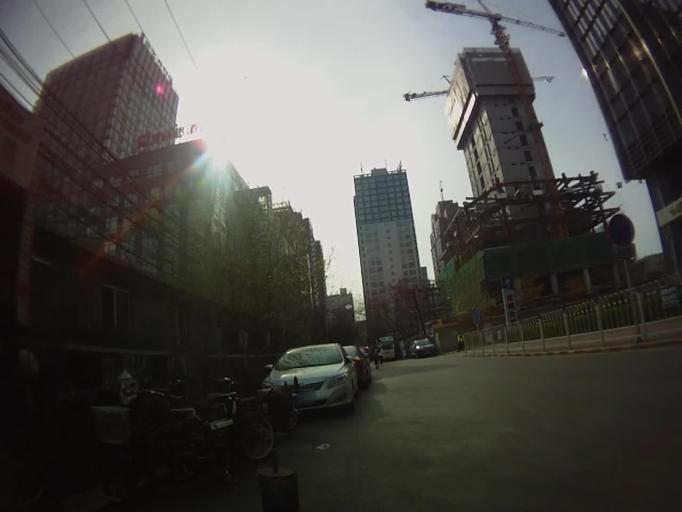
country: CN
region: Beijing
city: Chaowai
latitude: 39.9061
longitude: 116.4399
